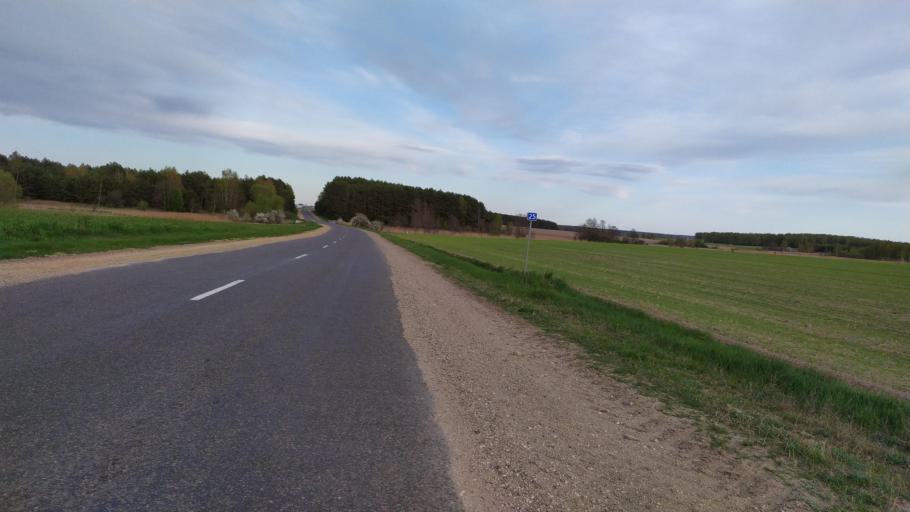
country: BY
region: Brest
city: Kamyanyets
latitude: 52.4096
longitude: 23.7283
